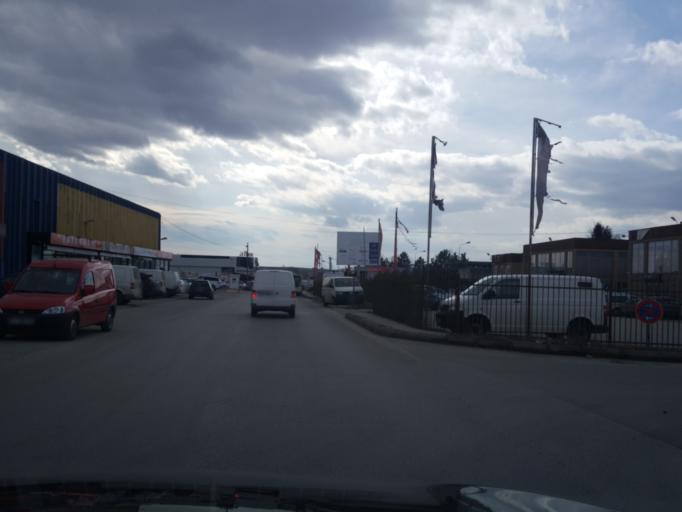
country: XK
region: Pristina
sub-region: Kosovo Polje
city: Kosovo Polje
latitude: 42.6458
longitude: 21.1284
